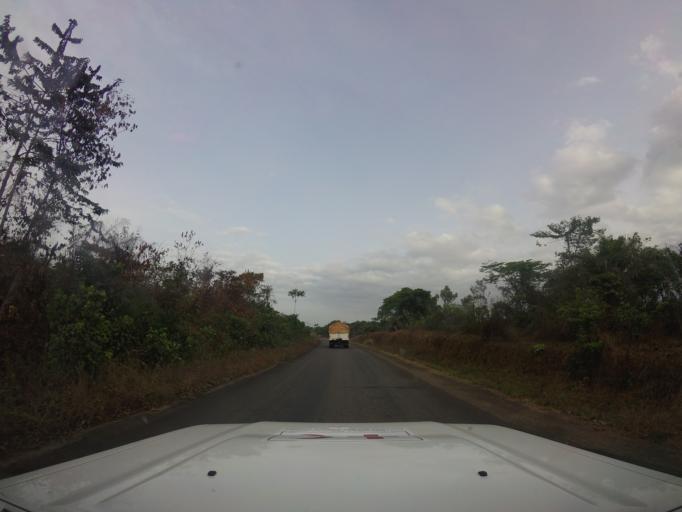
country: LR
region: Grand Cape Mount
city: Robertsport
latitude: 6.7488
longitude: -11.1307
